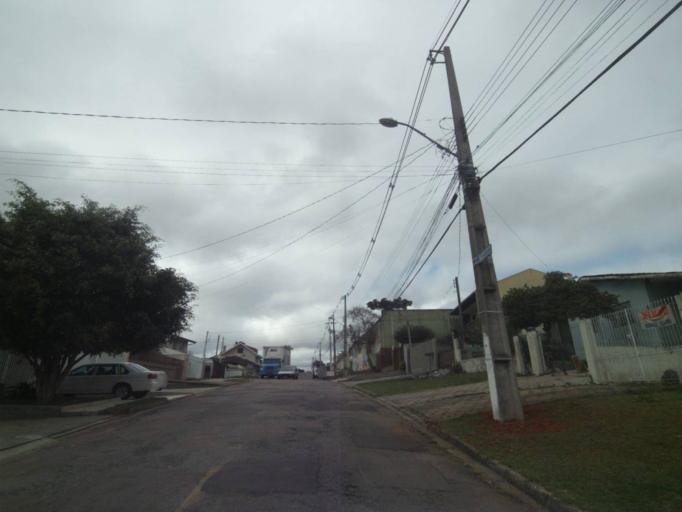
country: BR
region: Parana
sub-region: Sao Jose Dos Pinhais
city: Sao Jose dos Pinhais
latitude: -25.5290
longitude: -49.2930
